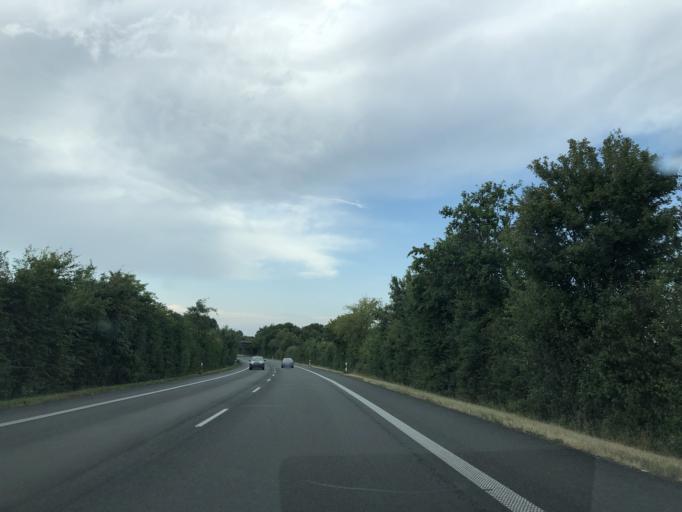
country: DE
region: North Rhine-Westphalia
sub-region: Regierungsbezirk Dusseldorf
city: Kranenburg
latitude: 51.7588
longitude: 6.0371
